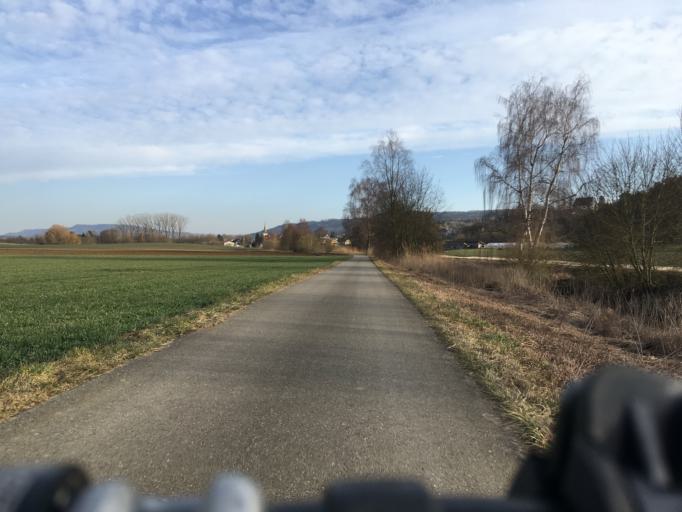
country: DE
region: Baden-Wuerttemberg
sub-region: Freiburg Region
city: Gailingen
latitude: 47.7279
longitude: 8.7450
